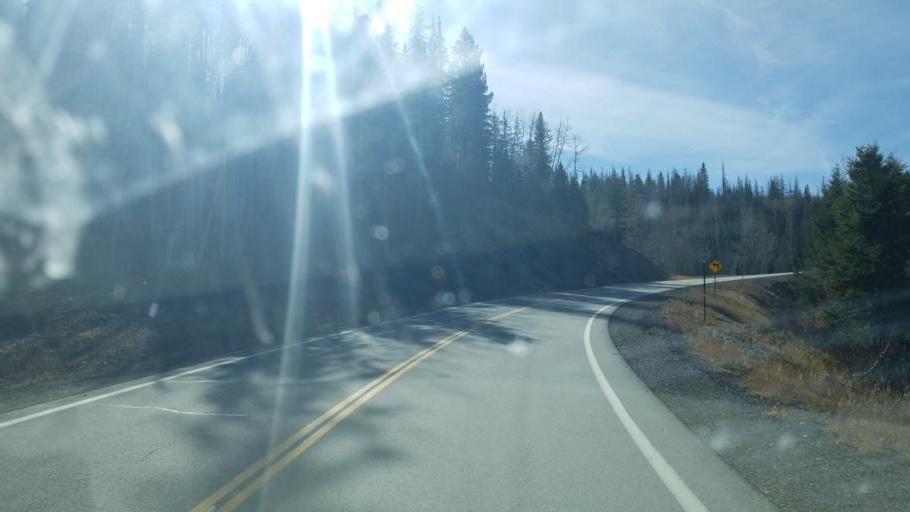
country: US
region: New Mexico
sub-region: Rio Arriba County
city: Chama
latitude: 37.1051
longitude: -106.3699
